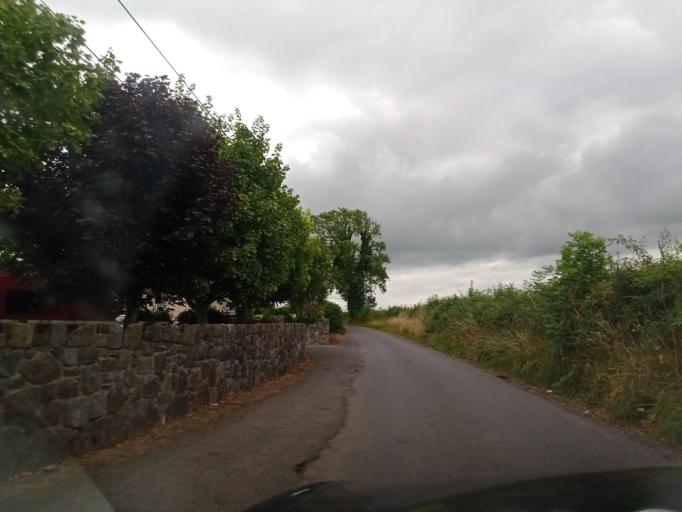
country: IE
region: Leinster
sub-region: Laois
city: Stradbally
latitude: 52.9823
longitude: -7.1664
